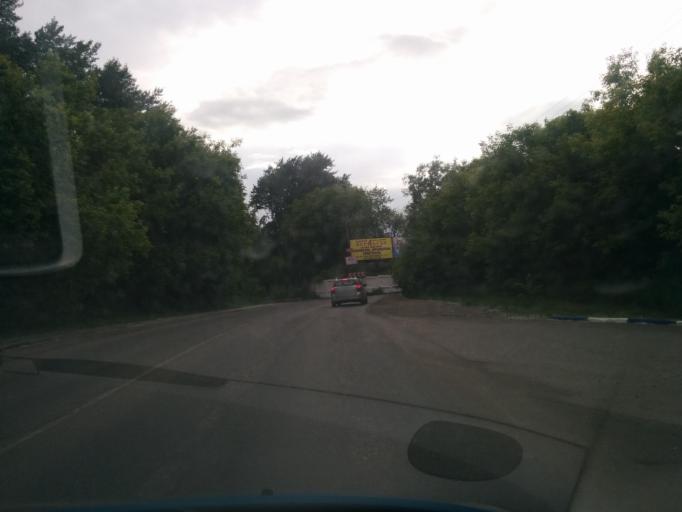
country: RU
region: Perm
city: Perm
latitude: 58.0031
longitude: 56.1832
